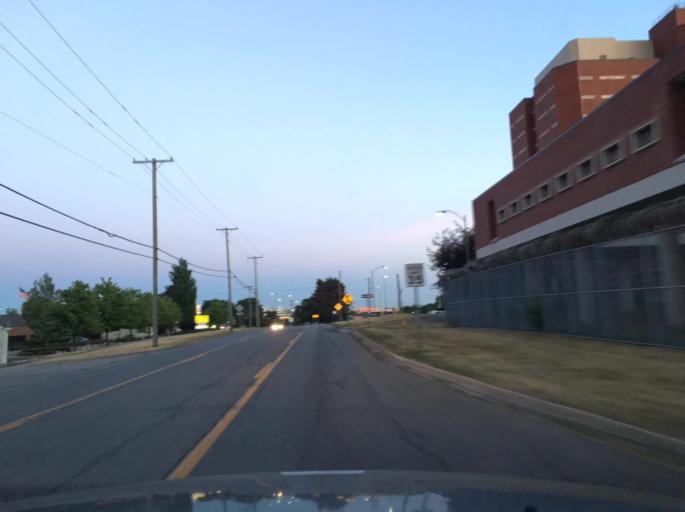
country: US
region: Michigan
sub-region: Macomb County
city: Mount Clemens
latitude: 42.6178
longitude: -82.8877
